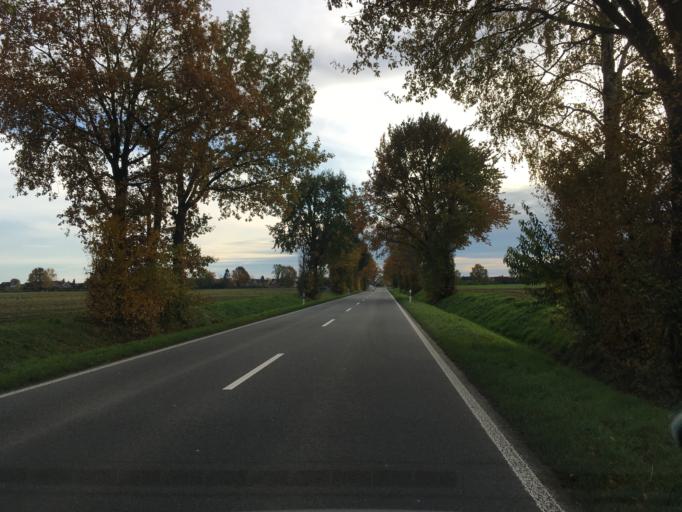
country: DE
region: North Rhine-Westphalia
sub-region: Regierungsbezirk Munster
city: Heiden
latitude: 51.8369
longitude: 6.9335
